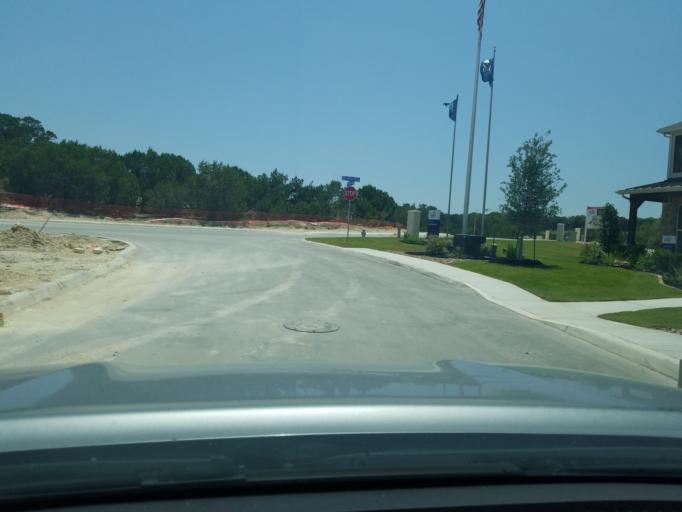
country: US
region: Texas
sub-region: Bexar County
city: Timberwood Park
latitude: 29.7073
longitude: -98.5053
